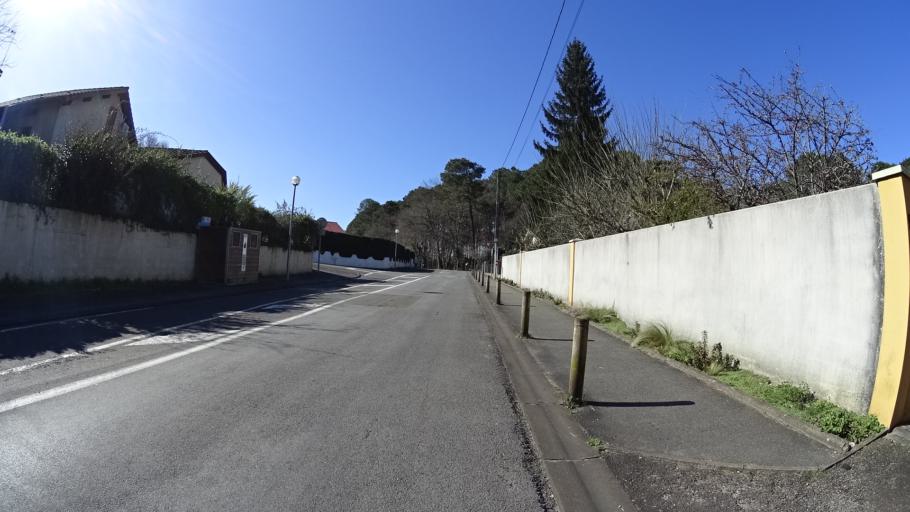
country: FR
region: Aquitaine
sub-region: Departement des Landes
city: Saint-Paul-les-Dax
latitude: 43.7337
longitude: -1.0748
